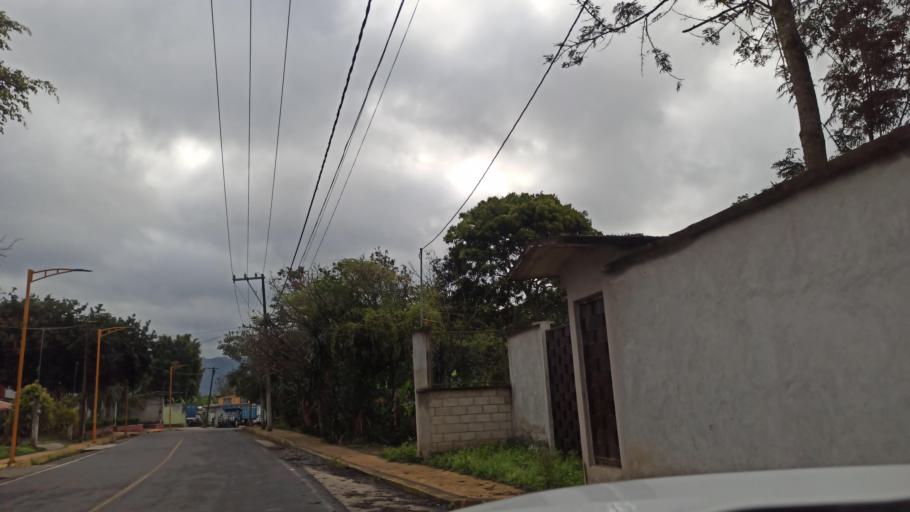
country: MX
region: Veracruz
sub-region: Chocaman
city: San Jose Neria
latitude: 19.0046
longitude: -97.0084
